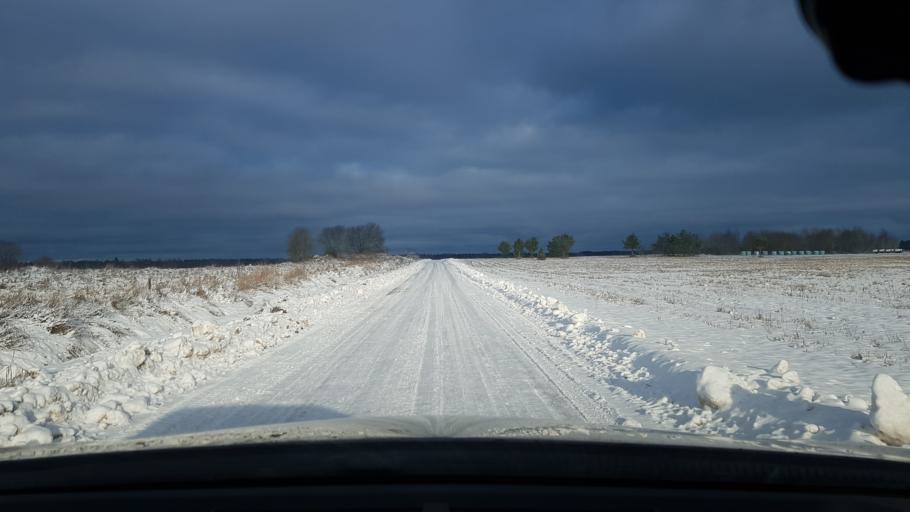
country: EE
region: Harju
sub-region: Keila linn
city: Keila
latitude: 59.3097
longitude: 24.2507
